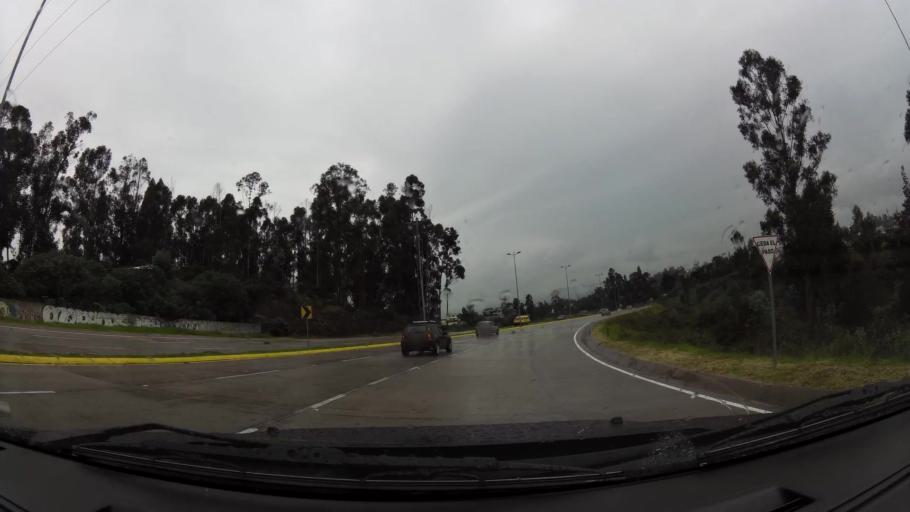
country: EC
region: Pichincha
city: Sangolqui
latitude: -0.2892
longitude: -78.4615
